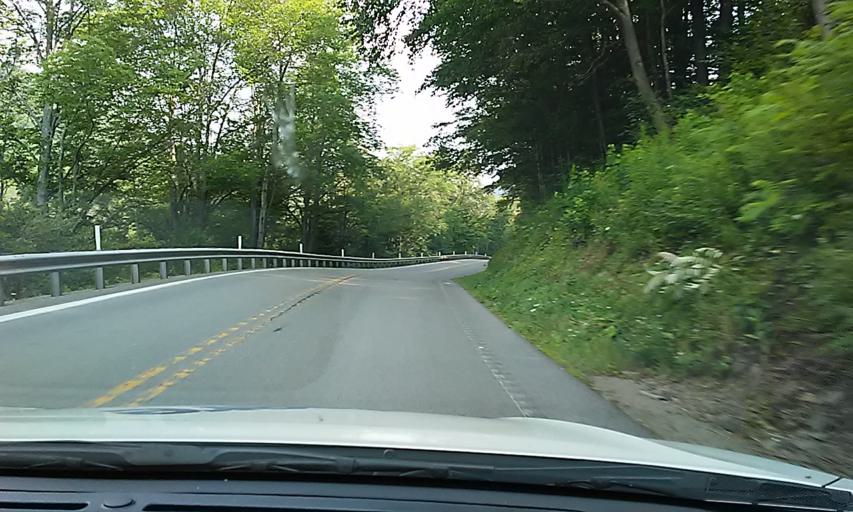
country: US
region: Pennsylvania
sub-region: Potter County
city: Galeton
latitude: 41.8219
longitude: -77.7961
